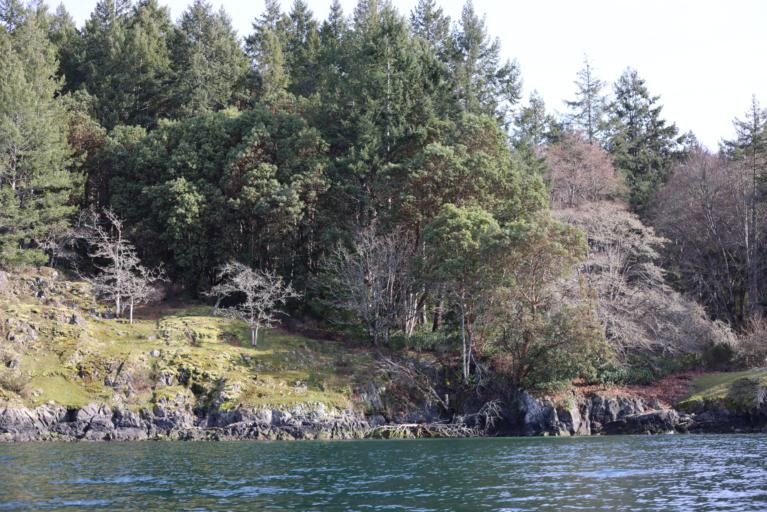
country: CA
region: British Columbia
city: Duncan
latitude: 48.7538
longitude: -123.5882
